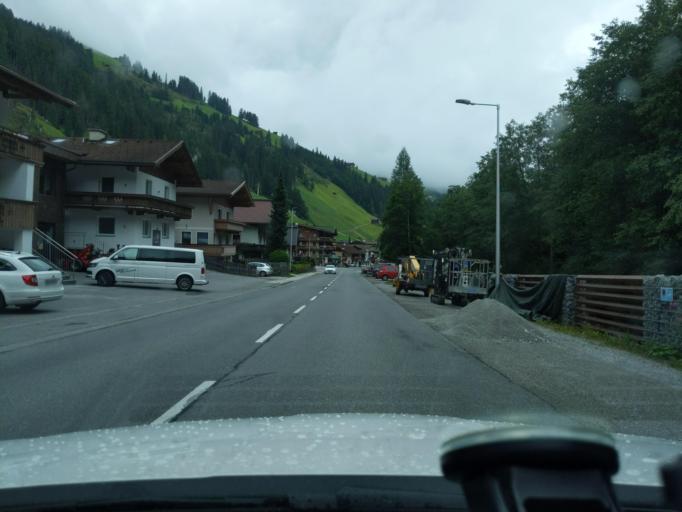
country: AT
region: Tyrol
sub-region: Politischer Bezirk Schwaz
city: Schwendau
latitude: 47.1522
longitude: 11.7249
